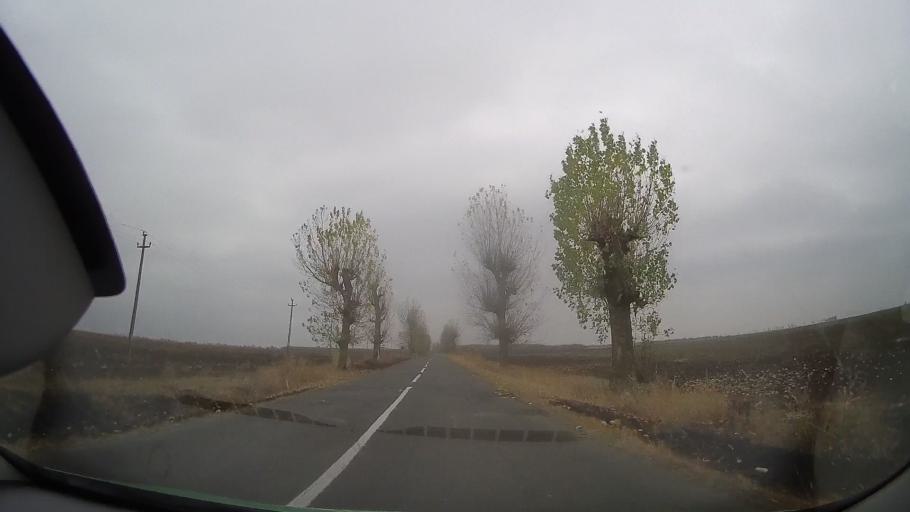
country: RO
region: Ialomita
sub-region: Comuna Grindu
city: Grindu
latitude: 44.7913
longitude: 26.9004
